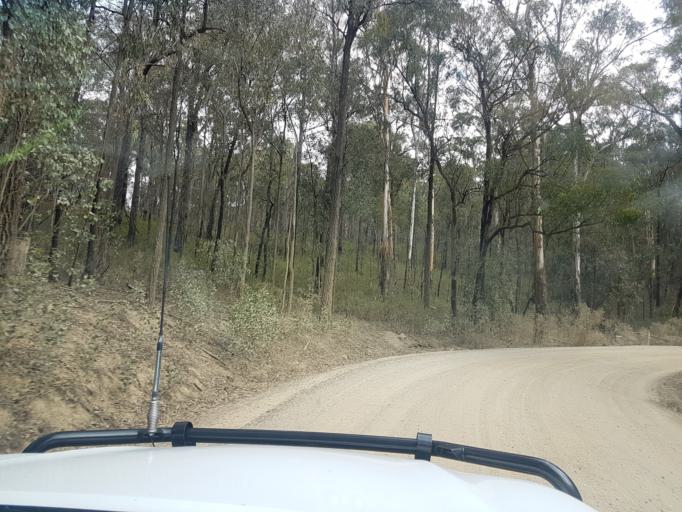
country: AU
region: Victoria
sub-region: East Gippsland
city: Bairnsdale
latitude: -37.6983
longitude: 147.5751
